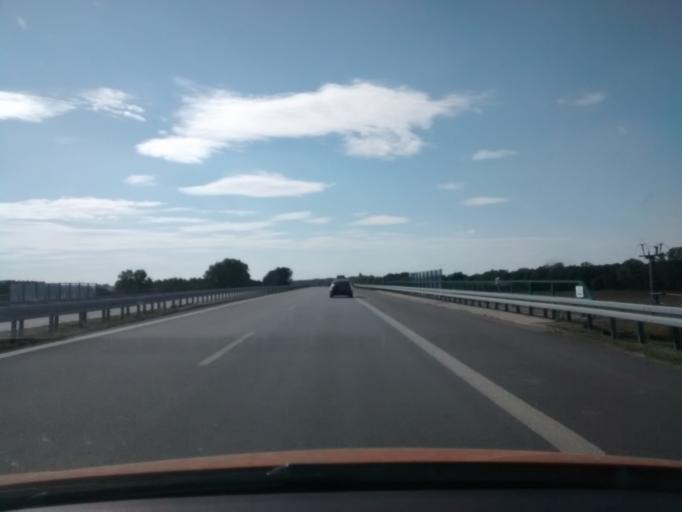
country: DE
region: Brandenburg
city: Trebbin
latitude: 52.2284
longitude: 13.2398
